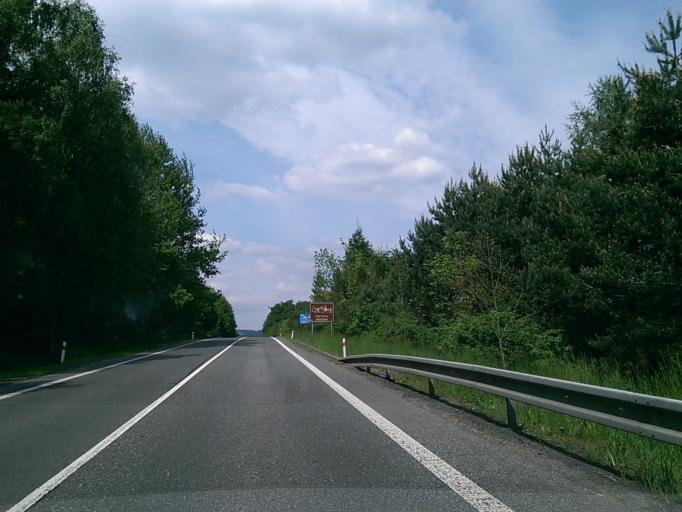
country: CZ
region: Liberecky
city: Mala Skala
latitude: 50.6294
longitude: 15.1852
